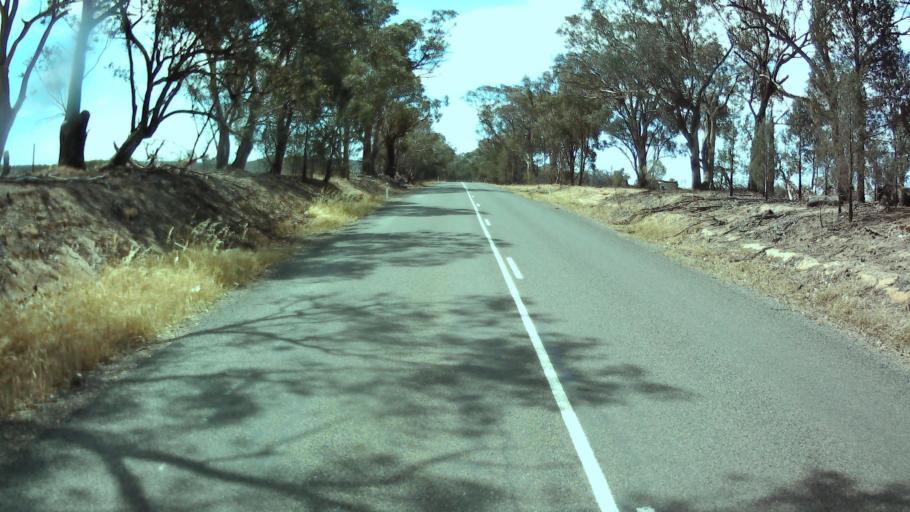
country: AU
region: New South Wales
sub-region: Weddin
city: Grenfell
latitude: -33.7843
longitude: 148.2097
